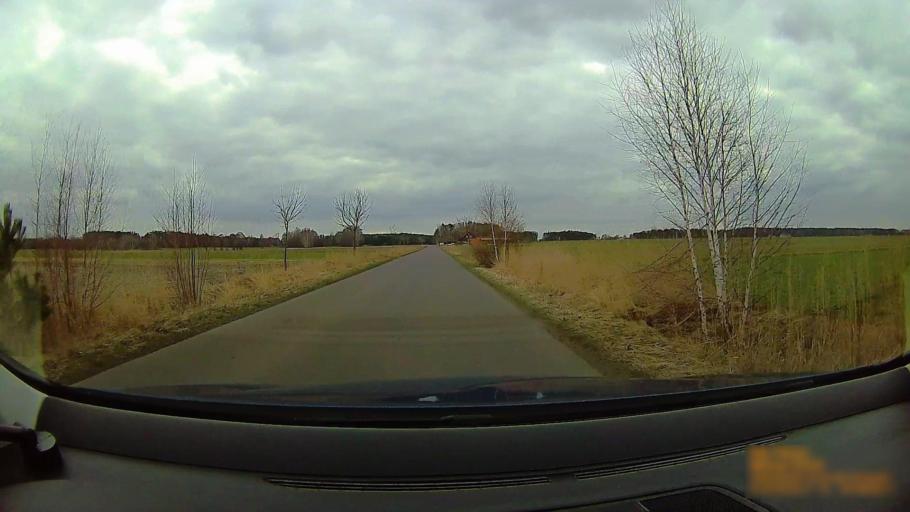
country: PL
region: Greater Poland Voivodeship
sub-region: Powiat koninski
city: Rychwal
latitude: 52.0902
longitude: 18.1406
